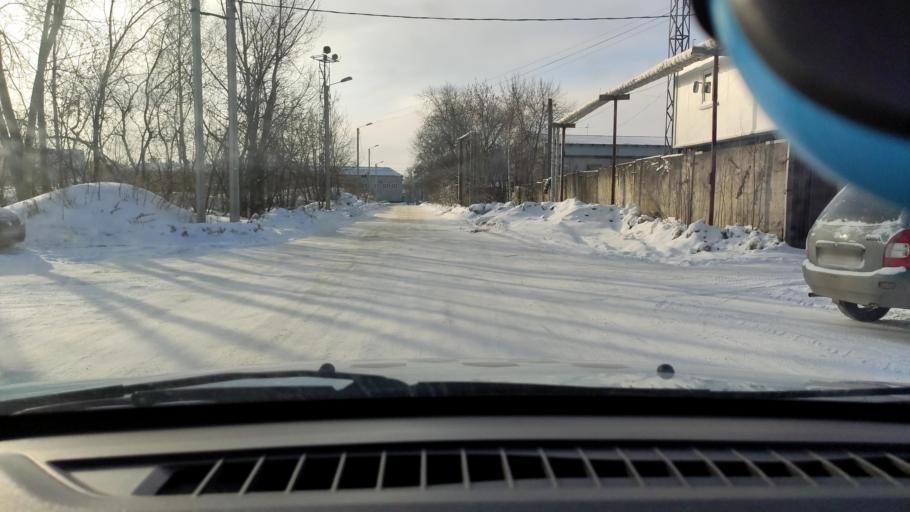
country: RU
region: Perm
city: Kultayevo
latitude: 57.9945
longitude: 55.9247
